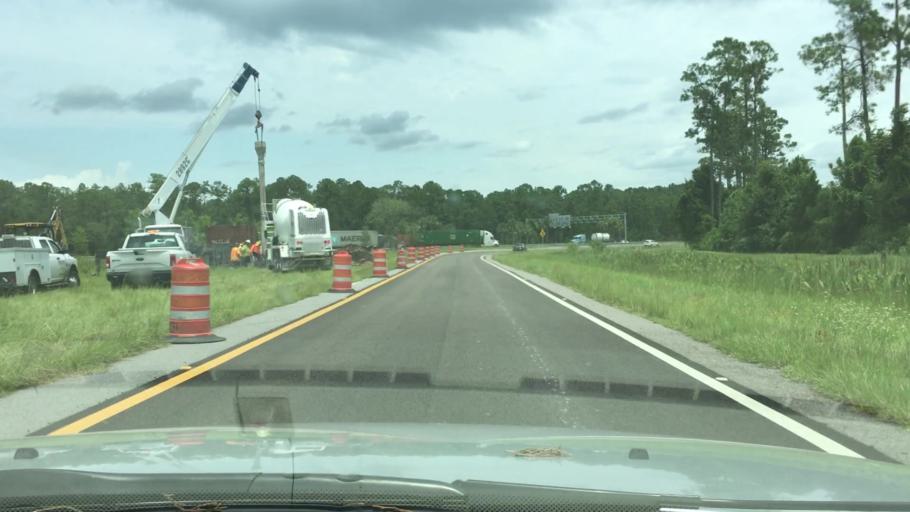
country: US
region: Florida
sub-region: Volusia County
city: Lake Helen
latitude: 29.0194
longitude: -81.2281
